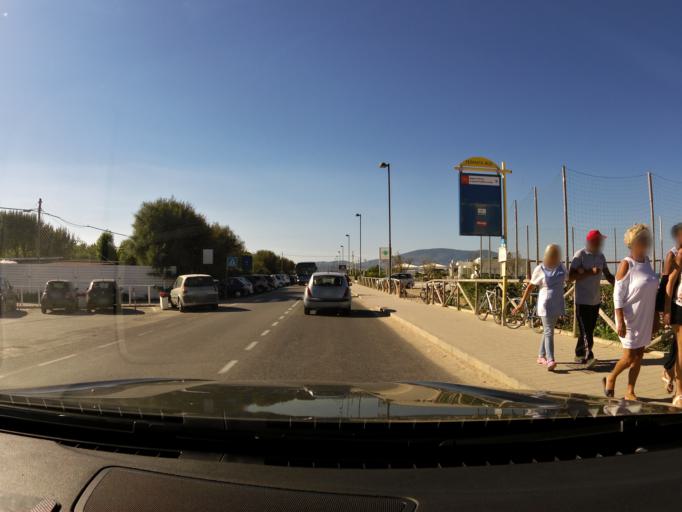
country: IT
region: The Marches
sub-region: Provincia di Ancona
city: Loreto Stazione
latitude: 43.4665
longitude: 13.6457
